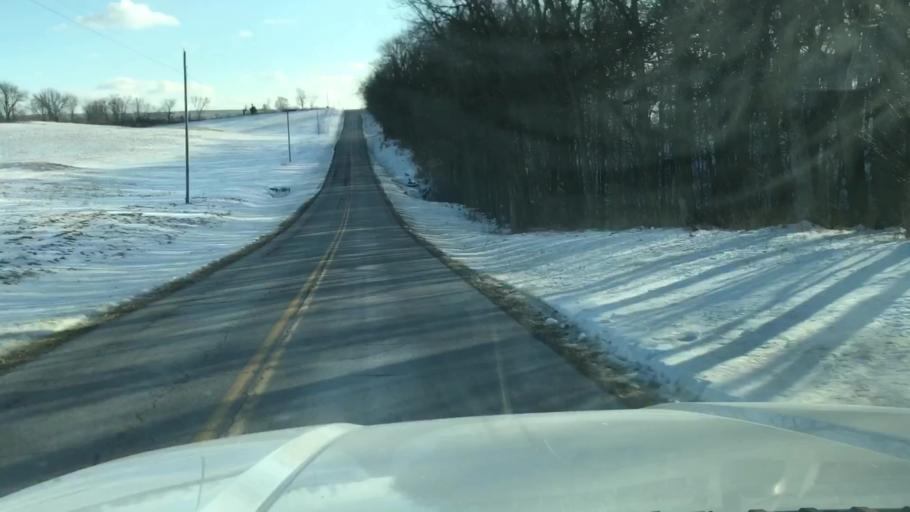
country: US
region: Missouri
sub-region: Holt County
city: Oregon
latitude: 40.0680
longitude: -94.9748
